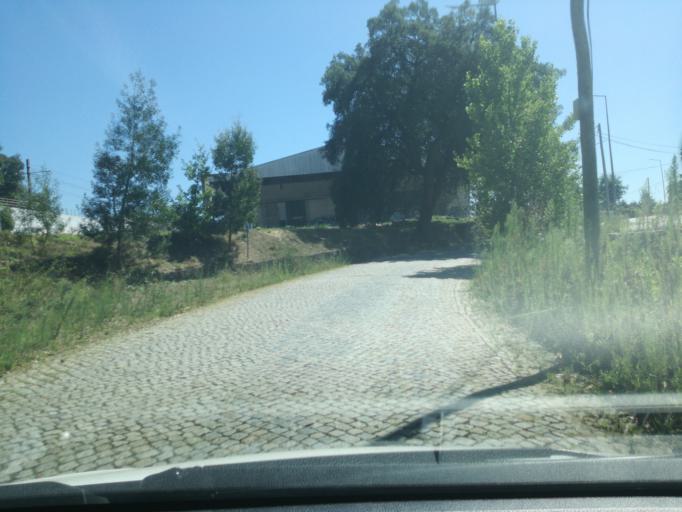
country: PT
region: Porto
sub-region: Maia
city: Maia
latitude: 41.2275
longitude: -8.6330
